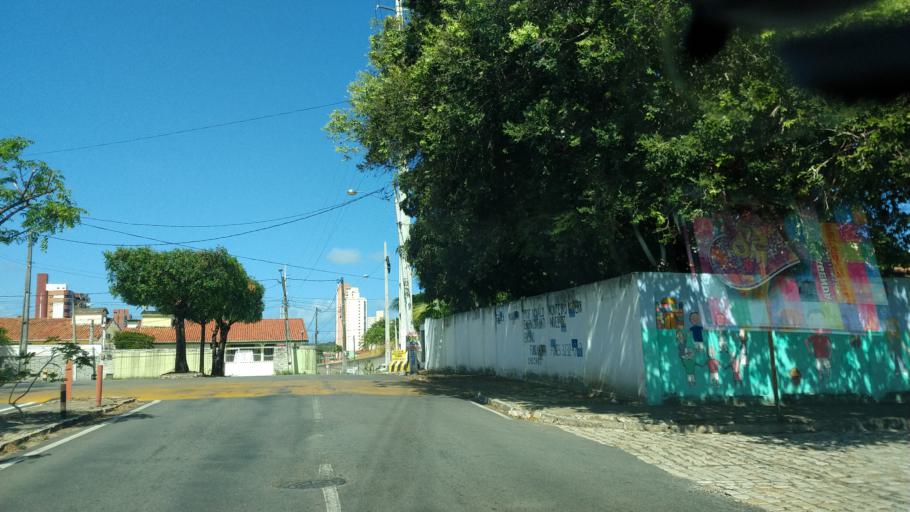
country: BR
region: Rio Grande do Norte
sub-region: Natal
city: Natal
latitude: -5.8689
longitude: -35.1979
